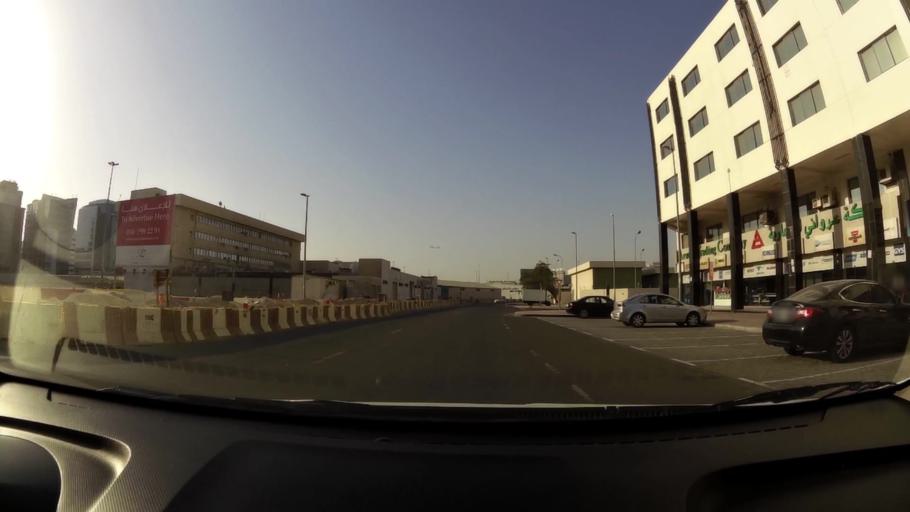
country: AE
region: Ash Shariqah
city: Sharjah
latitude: 25.2529
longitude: 55.3378
